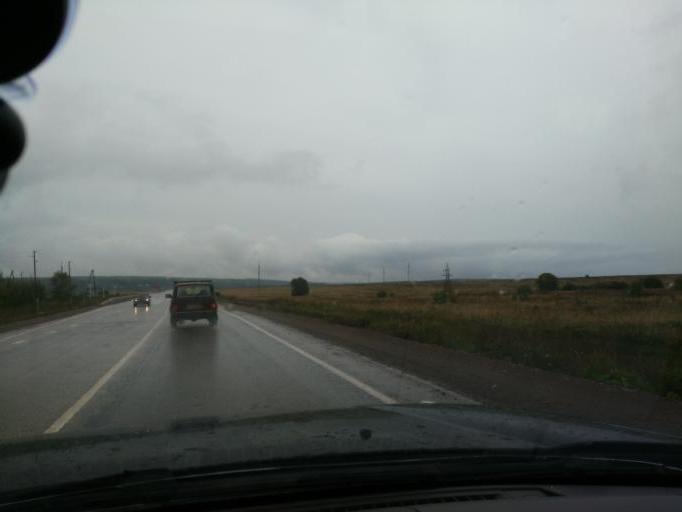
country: RU
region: Perm
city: Yugo-Kamskiy
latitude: 57.6994
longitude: 55.6216
